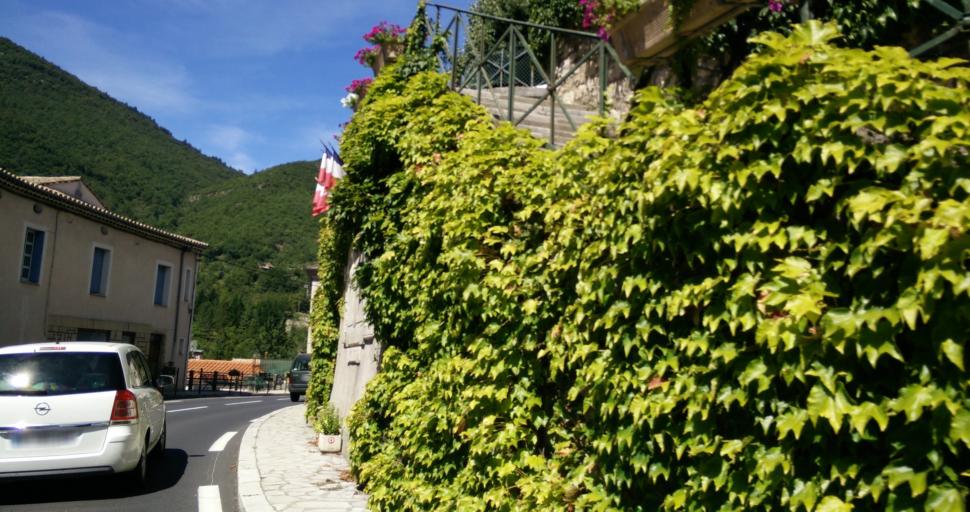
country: FR
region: Languedoc-Roussillon
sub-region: Departement du Gard
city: Aveze
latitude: 43.9665
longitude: 3.5187
